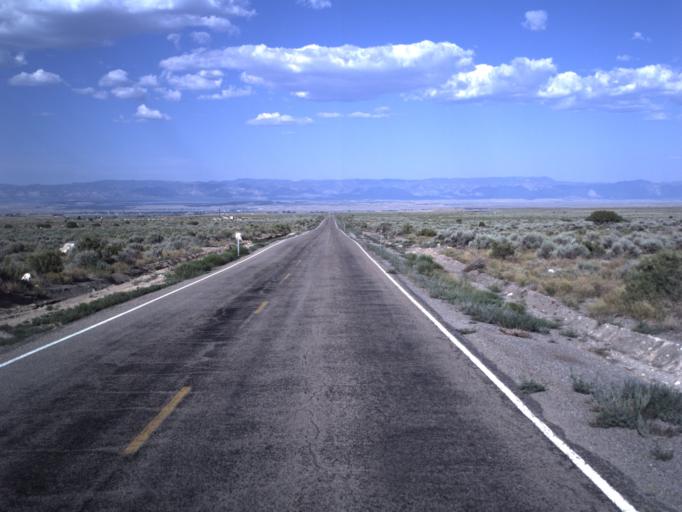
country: US
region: Utah
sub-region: Carbon County
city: Price
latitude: 39.4849
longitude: -110.8851
